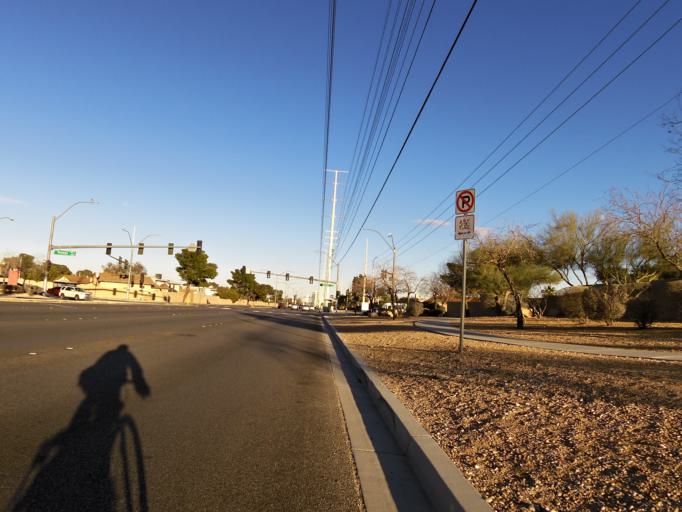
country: US
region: Nevada
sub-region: Clark County
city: Spring Valley
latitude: 36.1145
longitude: -115.2528
